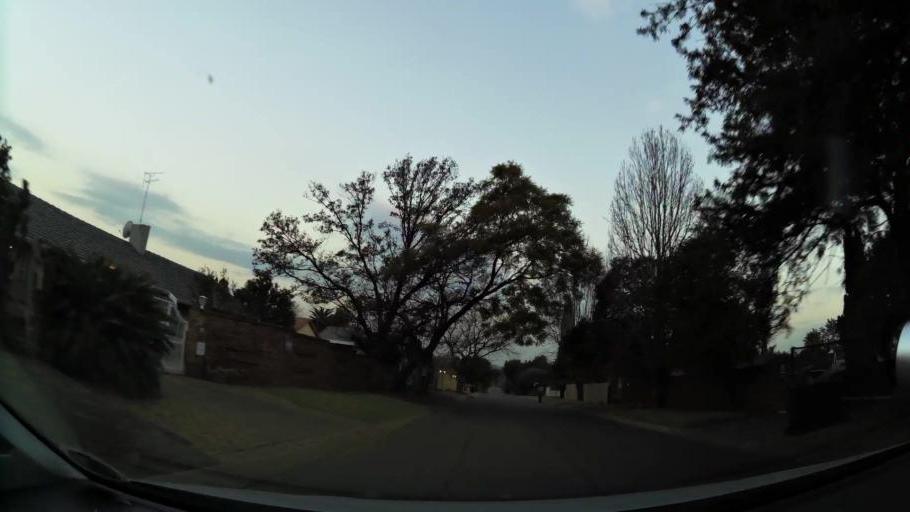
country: ZA
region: Gauteng
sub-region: Ekurhuleni Metropolitan Municipality
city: Tembisa
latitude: -26.0532
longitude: 28.2419
